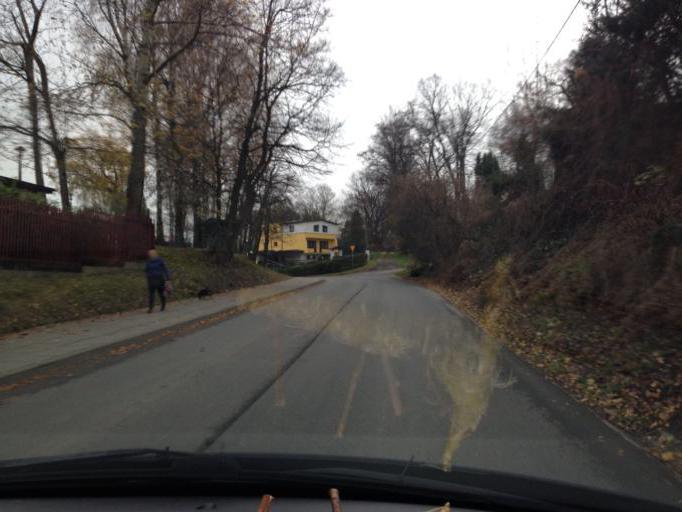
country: PL
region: Lesser Poland Voivodeship
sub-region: Powiat krakowski
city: Wrzasowice
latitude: 50.0034
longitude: 19.9495
